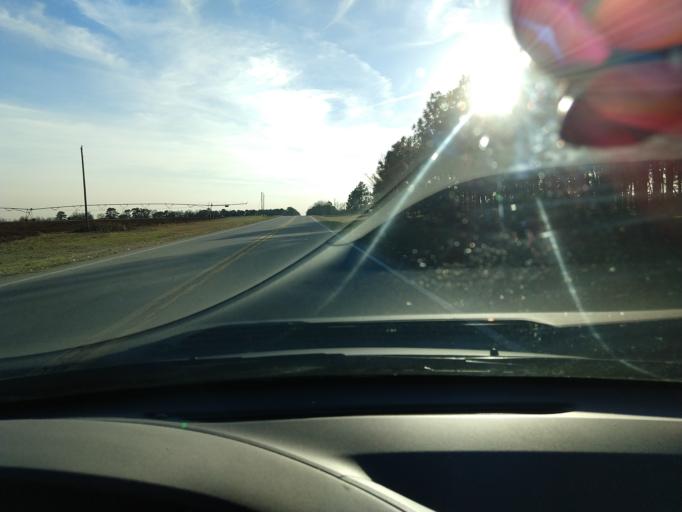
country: US
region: Georgia
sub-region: Sumter County
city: Americus
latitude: 32.1370
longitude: -84.1456
